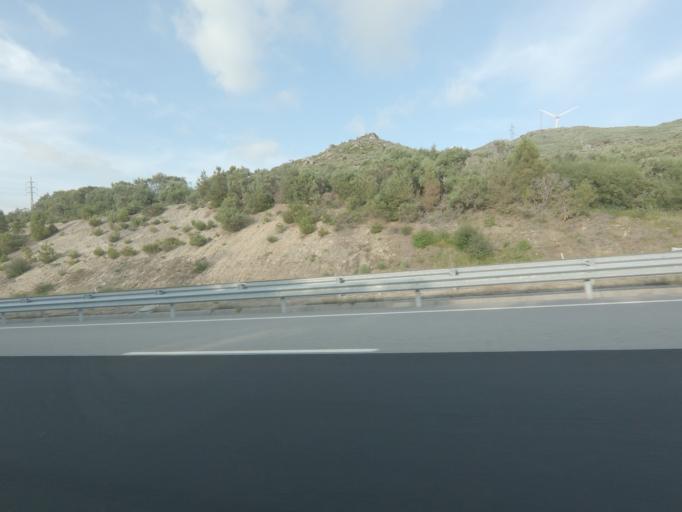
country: PT
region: Vila Real
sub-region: Vila Pouca de Aguiar
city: Vila Pouca de Aguiar
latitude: 41.4660
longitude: -7.6451
